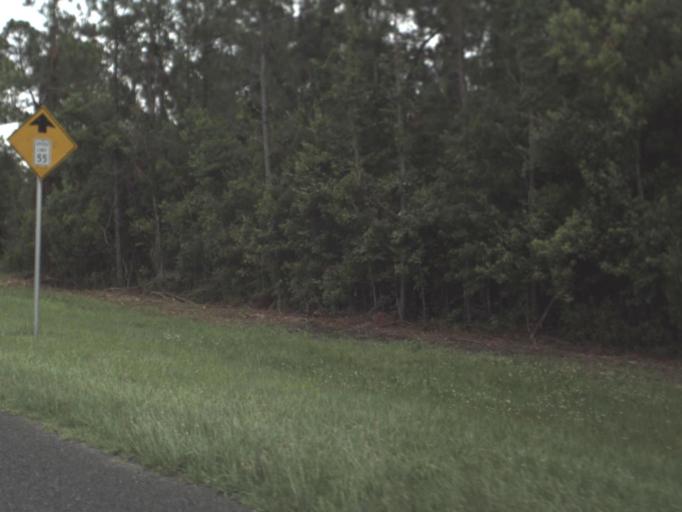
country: US
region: Florida
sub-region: Nassau County
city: Hilliard
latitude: 30.6707
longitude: -81.8964
